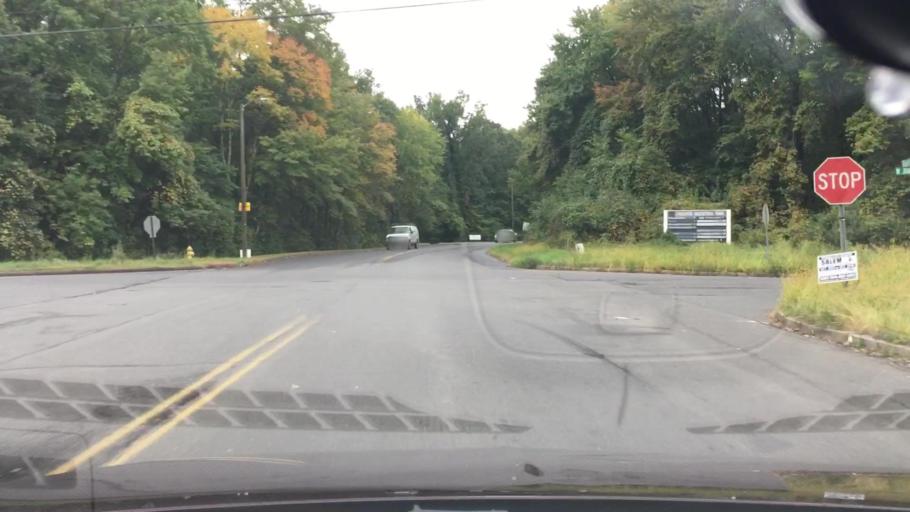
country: US
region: Connecticut
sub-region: New Haven County
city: Cheshire Village
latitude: 41.5576
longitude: -72.9136
